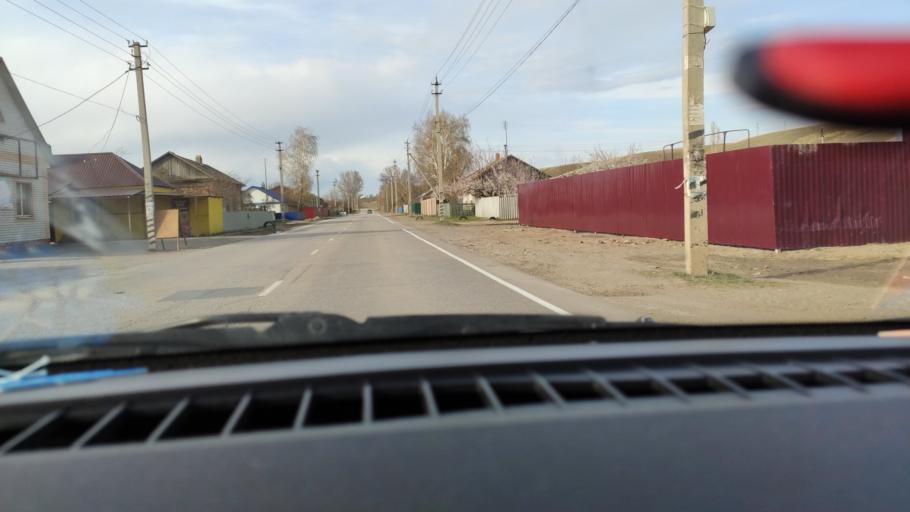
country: RU
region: Saratov
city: Privolzhskiy
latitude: 51.2112
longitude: 45.9194
